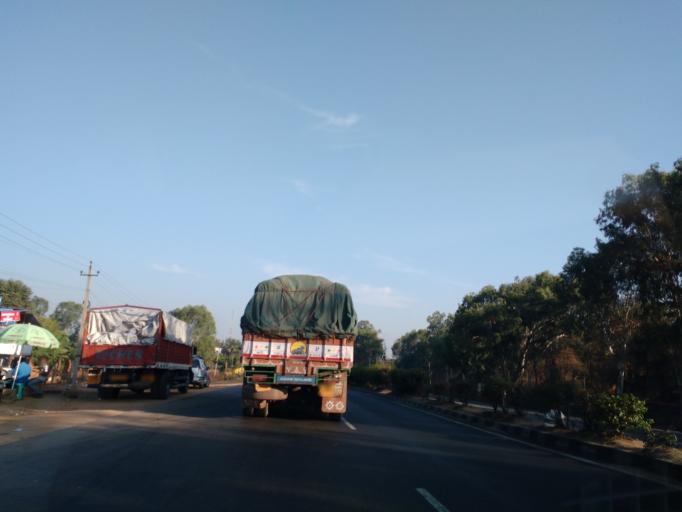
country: IN
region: Karnataka
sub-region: Bangalore Rural
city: Nelamangala
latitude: 13.1174
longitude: 77.3718
